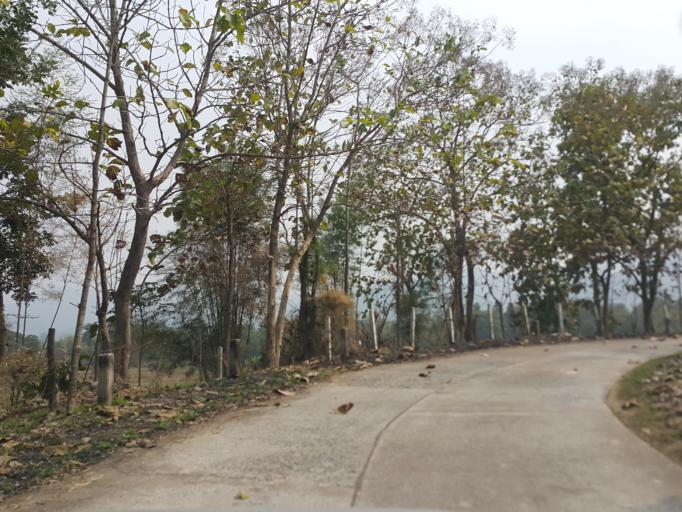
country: TH
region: Lampang
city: Thoen
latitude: 17.6342
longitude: 99.2567
